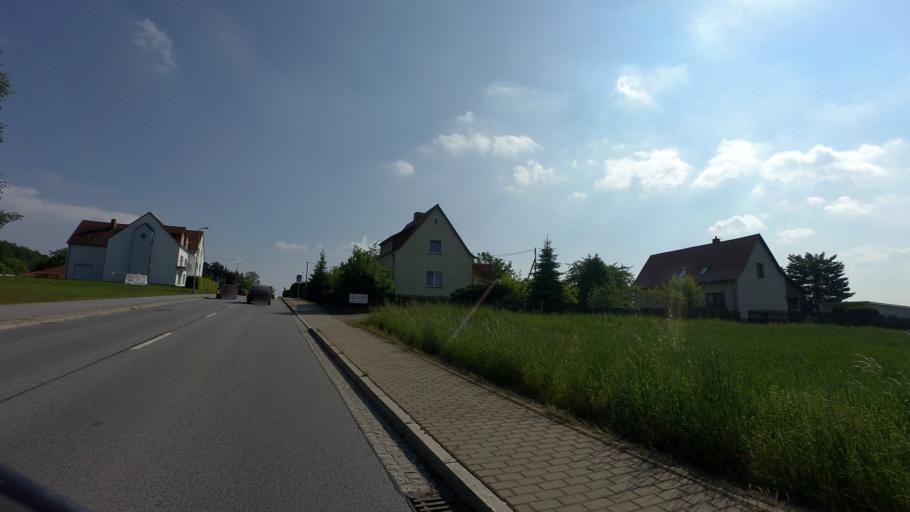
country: DE
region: Saxony
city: Grosspostwitz
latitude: 51.1375
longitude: 14.4417
